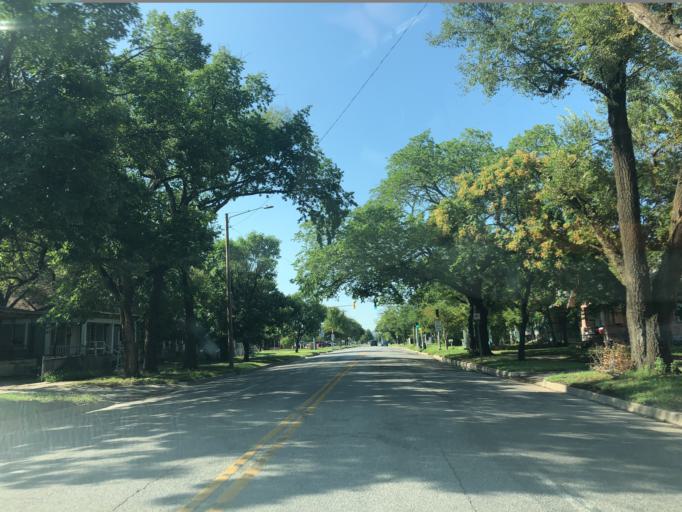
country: US
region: Kansas
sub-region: Sedgwick County
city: Wichita
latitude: 37.7037
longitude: -97.3420
